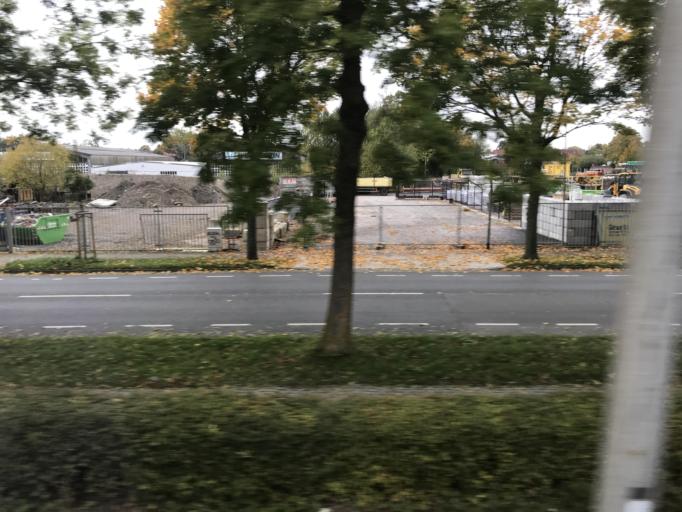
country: DE
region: Lower Saxony
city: Emden
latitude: 53.3580
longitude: 7.1977
